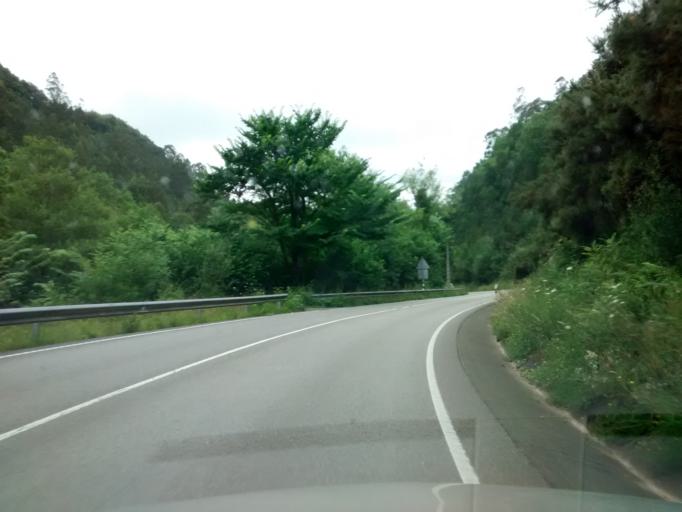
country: ES
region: Asturias
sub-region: Province of Asturias
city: Santa Eulalia
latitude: 43.4402
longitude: -5.4387
